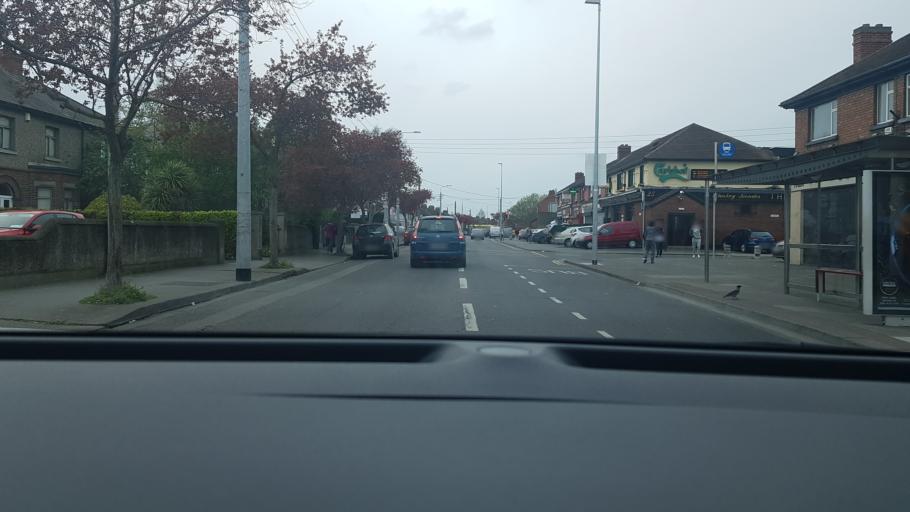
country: IE
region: Leinster
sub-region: South Dublin
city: Terenure
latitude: 53.3202
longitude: -6.2918
